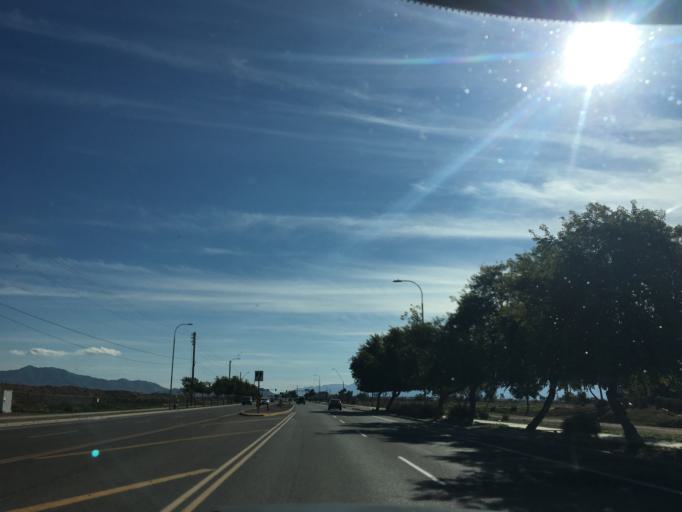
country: US
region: Arizona
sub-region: Maricopa County
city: Laveen
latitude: 33.4147
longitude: -112.1694
